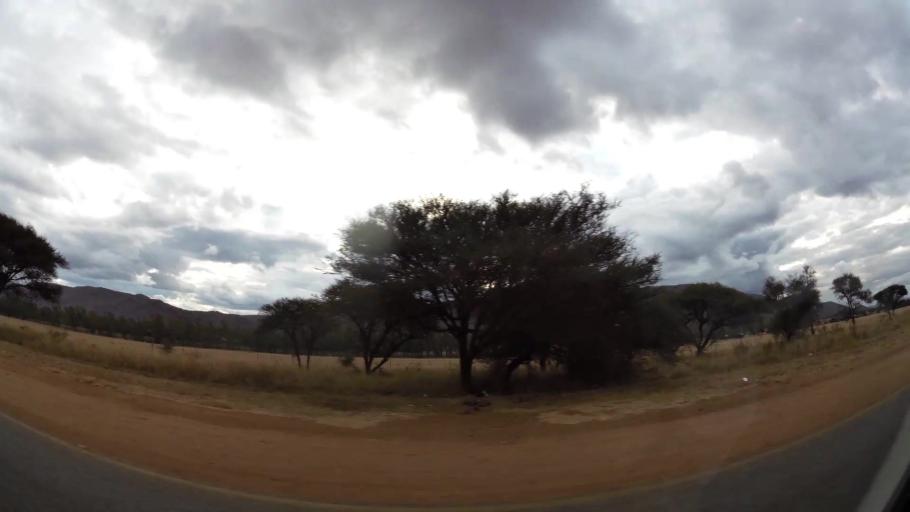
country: ZA
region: Limpopo
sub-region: Waterberg District Municipality
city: Mokopane
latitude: -24.2682
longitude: 28.9823
